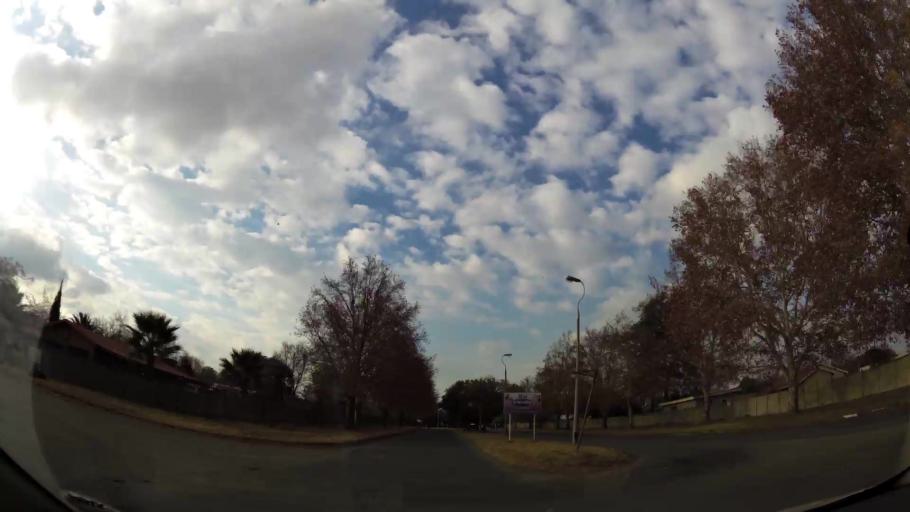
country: ZA
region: Orange Free State
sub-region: Fezile Dabi District Municipality
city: Sasolburg
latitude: -26.8118
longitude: 27.8207
